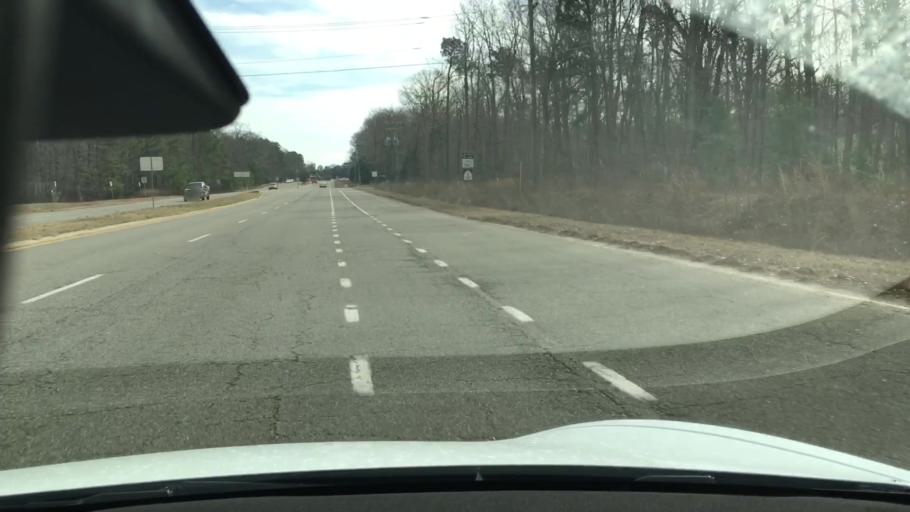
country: US
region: Virginia
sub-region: Chesterfield County
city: Bon Air
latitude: 37.5354
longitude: -77.6354
